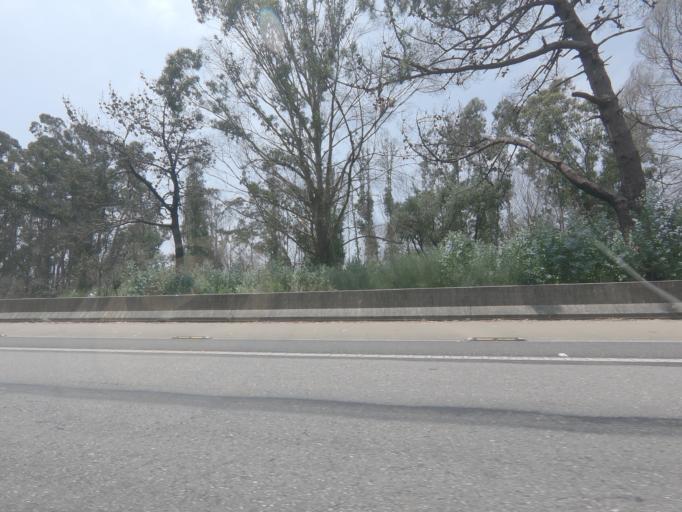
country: ES
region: Galicia
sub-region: Provincia de Pontevedra
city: A Guarda
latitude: 41.9268
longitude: -8.8812
